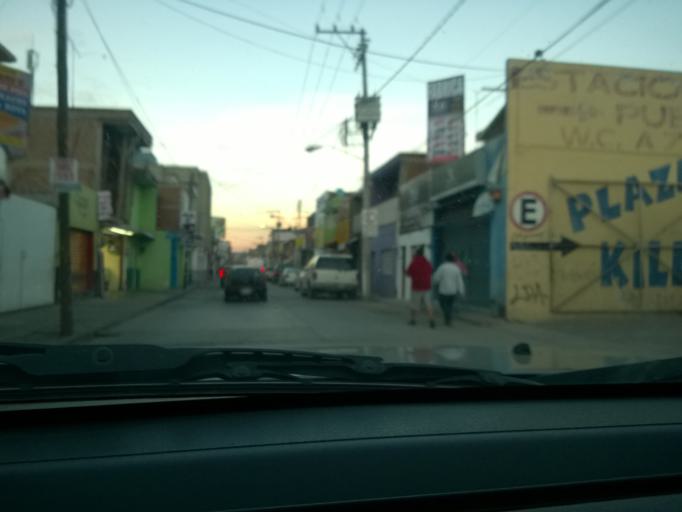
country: MX
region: Guanajuato
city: Leon
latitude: 21.1242
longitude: -101.6631
